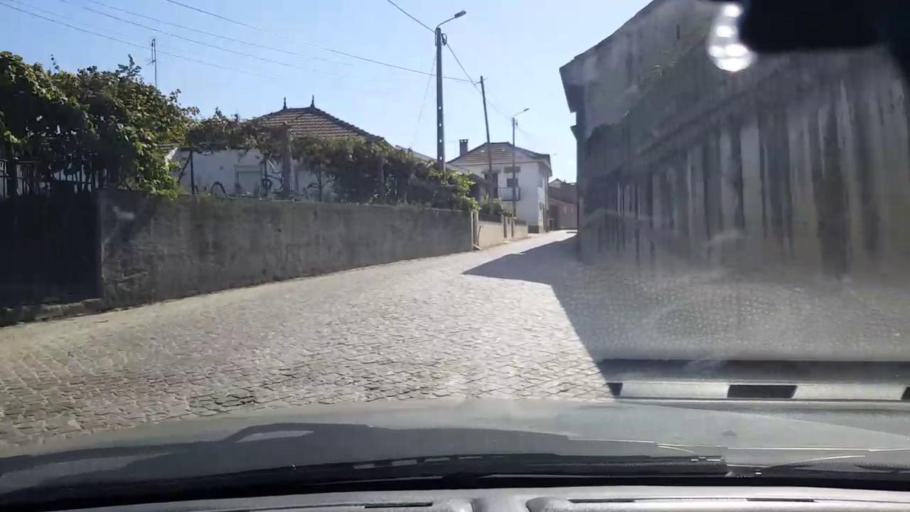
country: PT
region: Porto
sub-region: Matosinhos
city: Lavra
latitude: 41.2909
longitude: -8.6900
